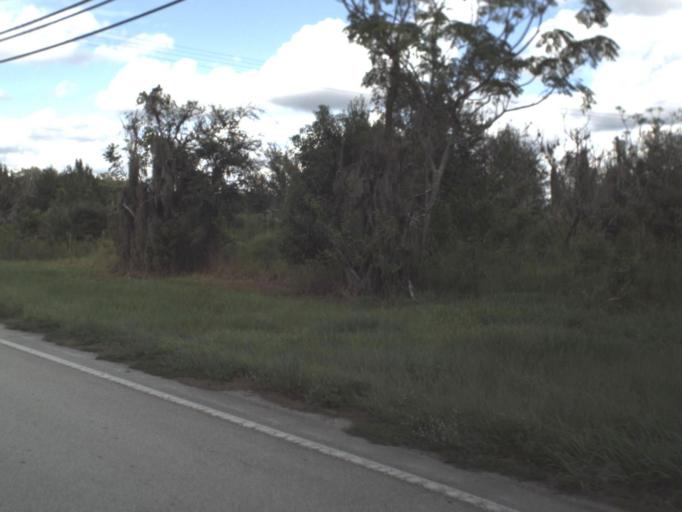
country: US
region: Florida
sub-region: Manatee County
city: Ellenton
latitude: 27.5846
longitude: -82.4255
